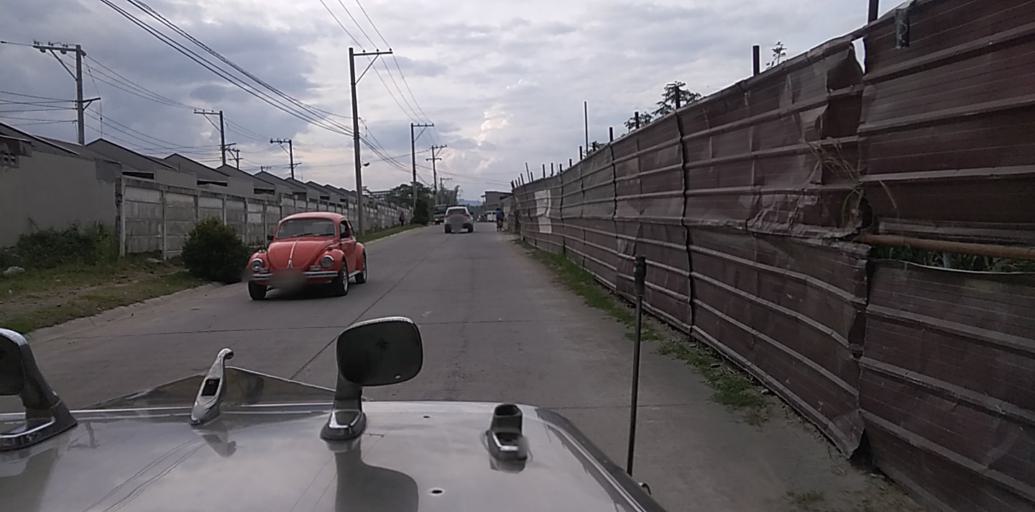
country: PH
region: Central Luzon
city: Santol
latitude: 15.1669
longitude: 120.5379
